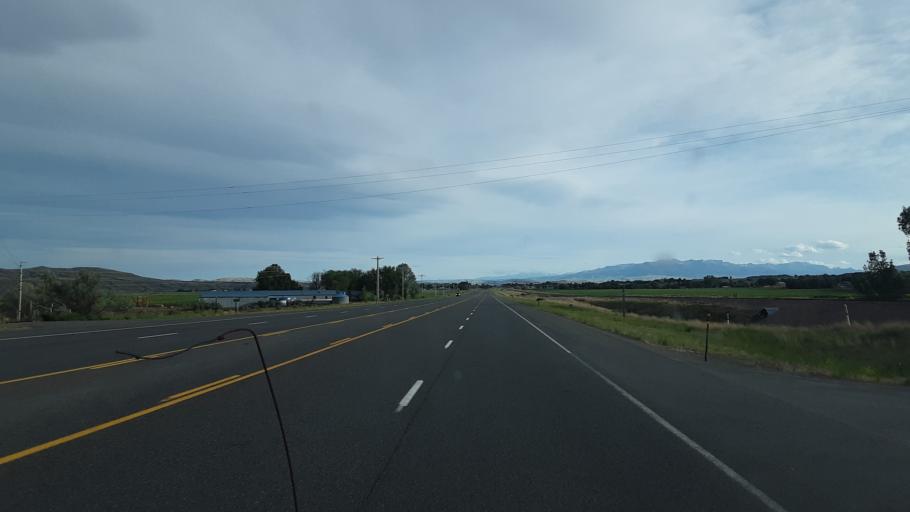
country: US
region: Wyoming
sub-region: Park County
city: Cody
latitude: 44.6235
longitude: -108.9564
